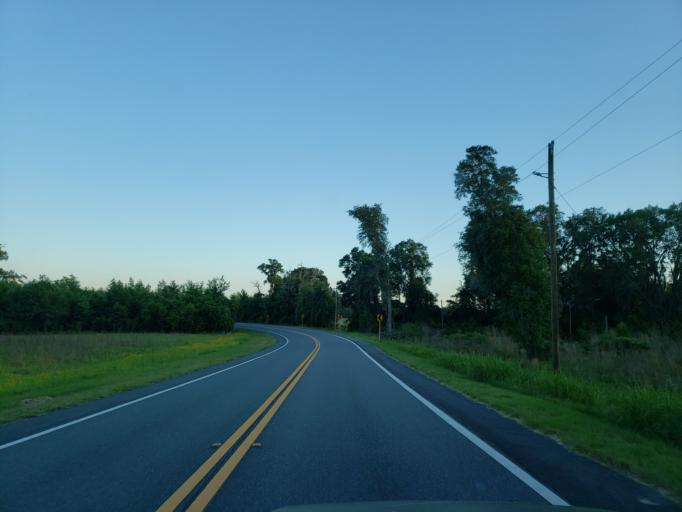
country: US
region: Florida
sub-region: Madison County
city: Madison
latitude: 30.5843
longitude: -83.2414
